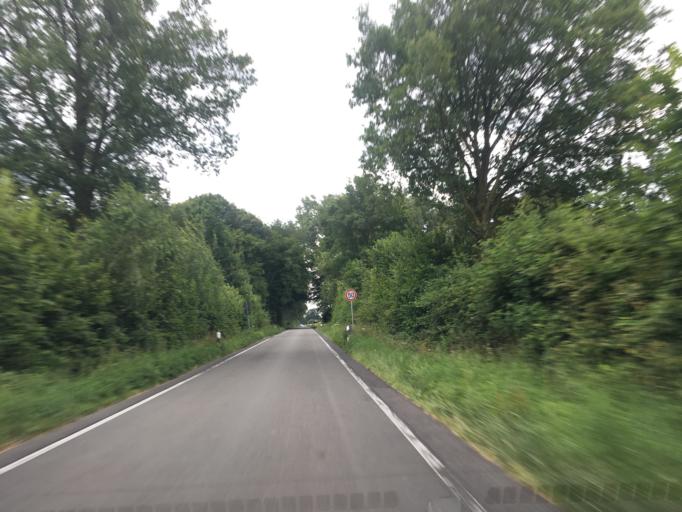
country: DE
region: North Rhine-Westphalia
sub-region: Regierungsbezirk Munster
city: Telgte
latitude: 51.9532
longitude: 7.7165
